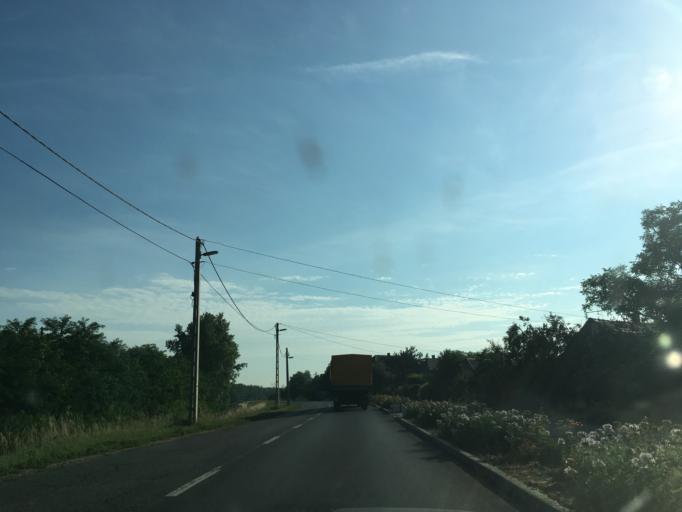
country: HU
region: Hajdu-Bihar
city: Hajdusamson
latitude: 47.6134
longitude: 21.7680
